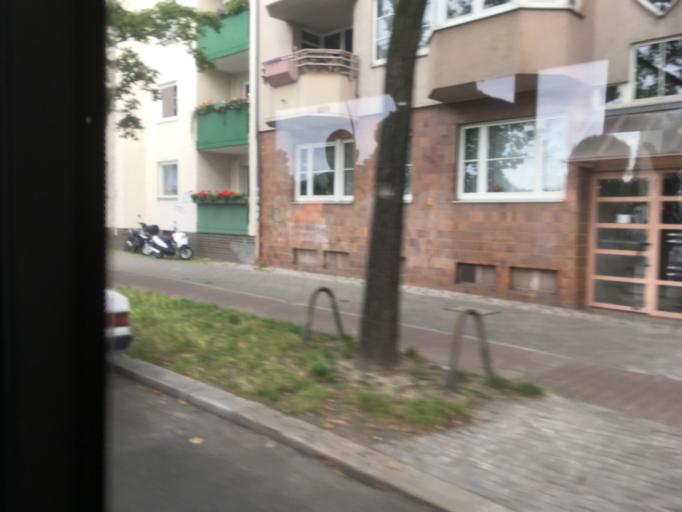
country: DE
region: Berlin
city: Wilhelmstadt
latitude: 52.5259
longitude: 13.1944
